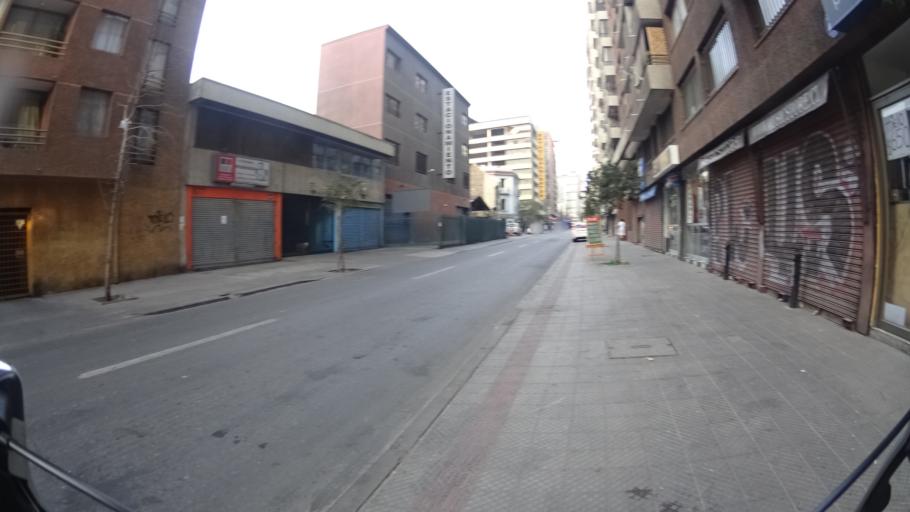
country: CL
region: Santiago Metropolitan
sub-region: Provincia de Santiago
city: Santiago
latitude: -33.4458
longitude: -70.6487
